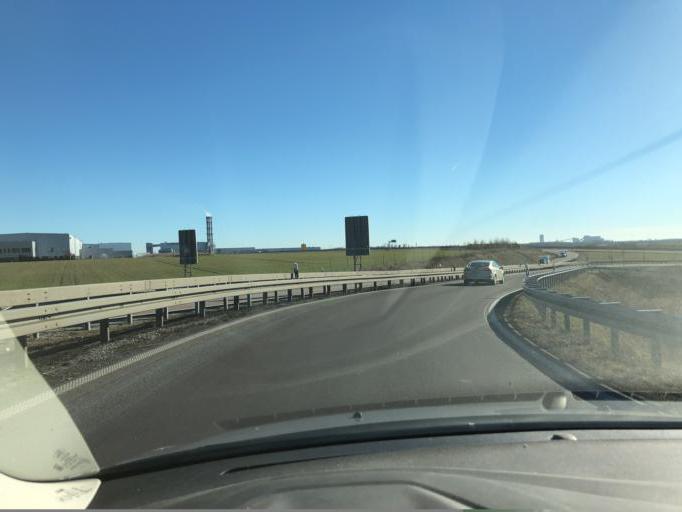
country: DE
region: Saxony-Anhalt
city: Ilberstedt
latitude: 51.8058
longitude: 11.6856
